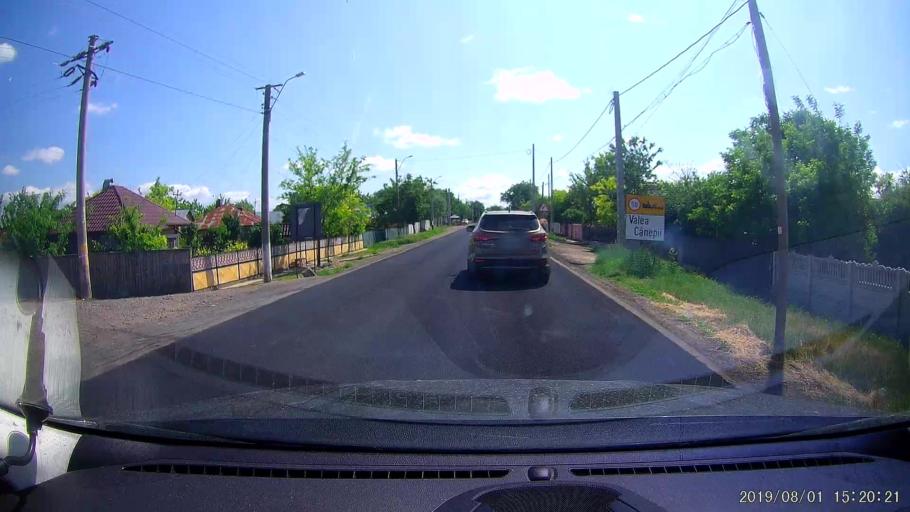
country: RO
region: Braila
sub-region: Comuna Tufesti
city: Tufesti
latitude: 45.0800
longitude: 27.8074
